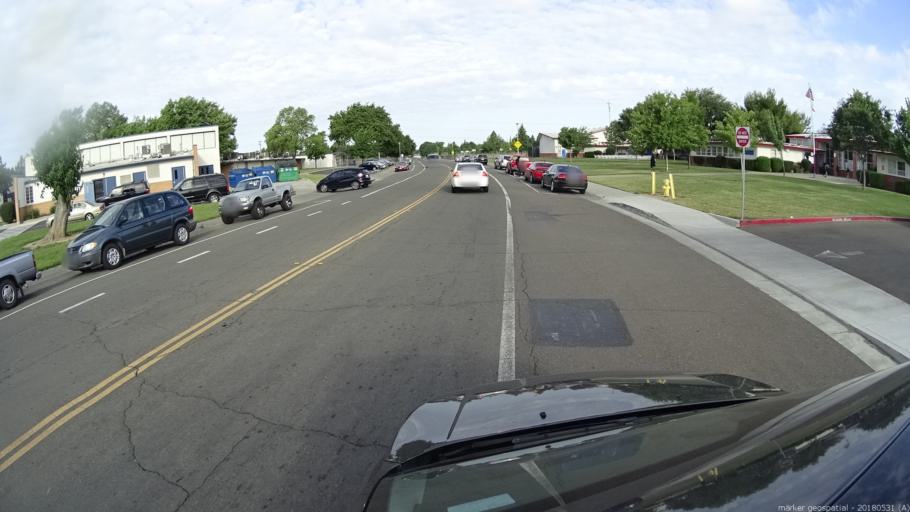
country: US
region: California
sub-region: Sacramento County
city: Sacramento
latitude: 38.6245
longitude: -121.4806
